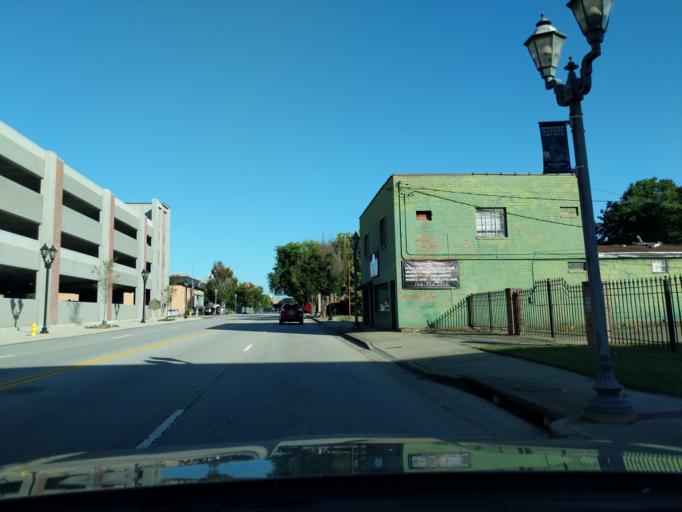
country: US
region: Georgia
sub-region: Richmond County
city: Augusta
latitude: 33.4789
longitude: -81.9713
